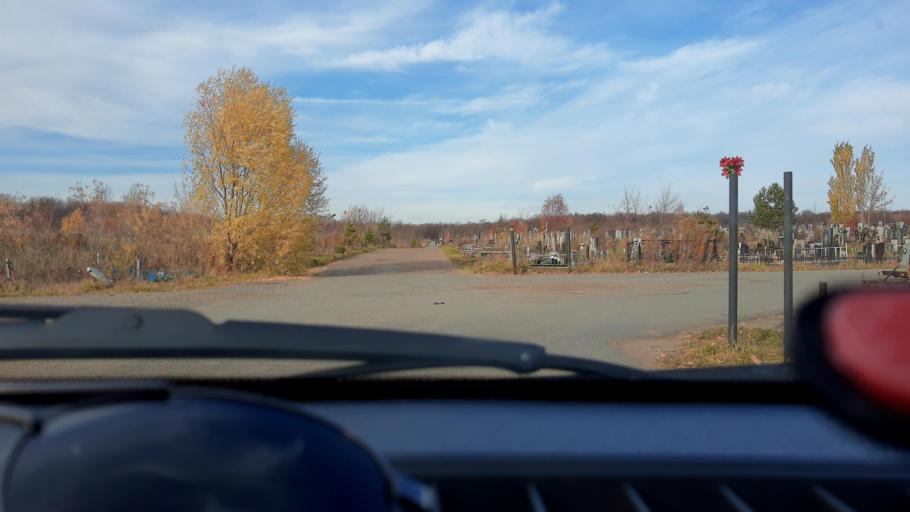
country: RU
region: Bashkortostan
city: Ufa
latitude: 54.8592
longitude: 56.1573
